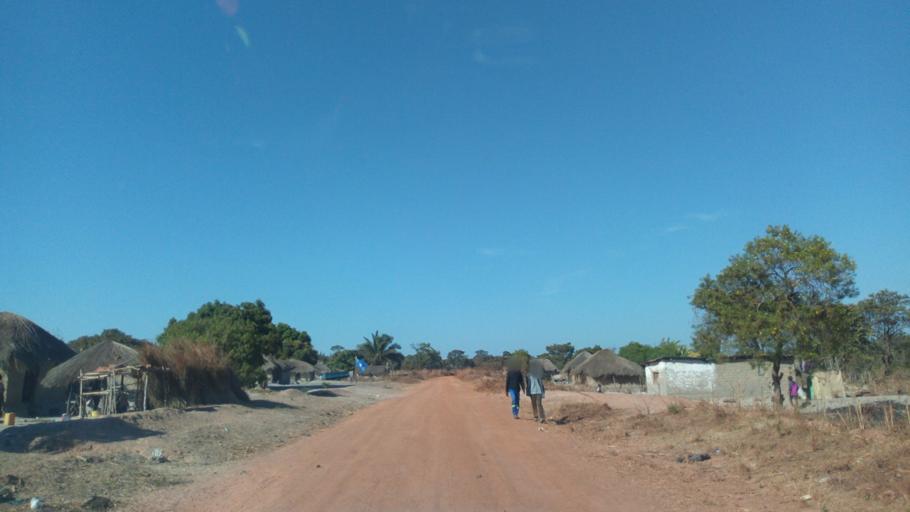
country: ZM
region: Luapula
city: Mwense
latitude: -10.6292
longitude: 28.4109
